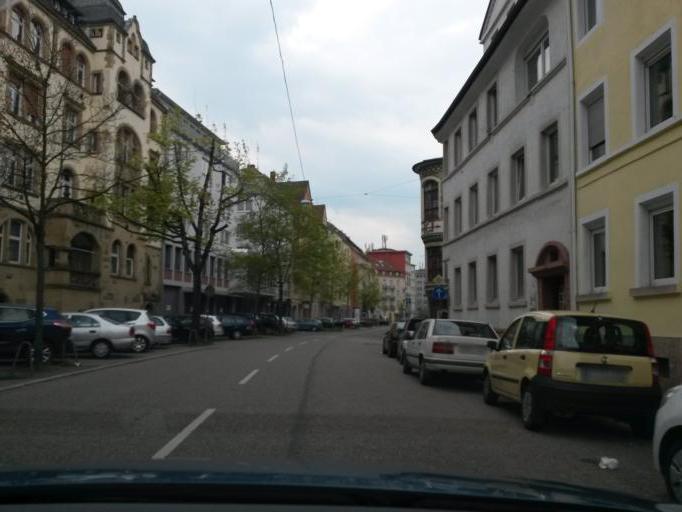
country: DE
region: Baden-Wuerttemberg
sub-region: Karlsruhe Region
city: Pforzheim
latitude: 48.8823
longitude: 8.6958
